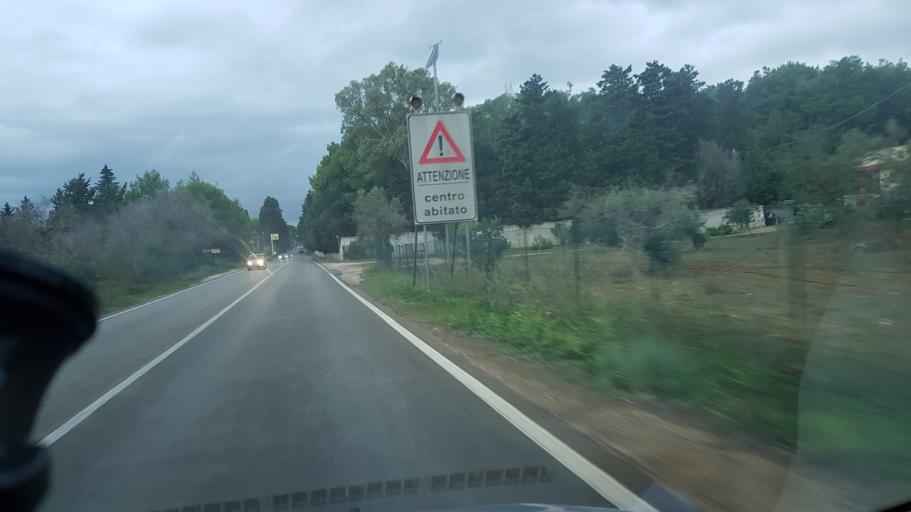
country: IT
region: Apulia
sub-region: Provincia di Lecce
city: Arnesano
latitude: 40.3628
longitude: 18.0872
